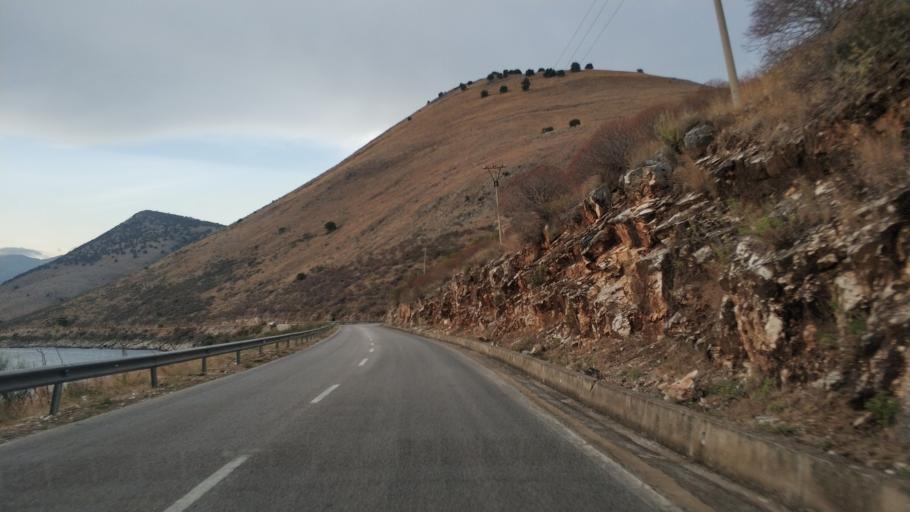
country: AL
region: Vlore
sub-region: Rrethi i Vlores
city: Himare
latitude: 40.0546
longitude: 19.8038
